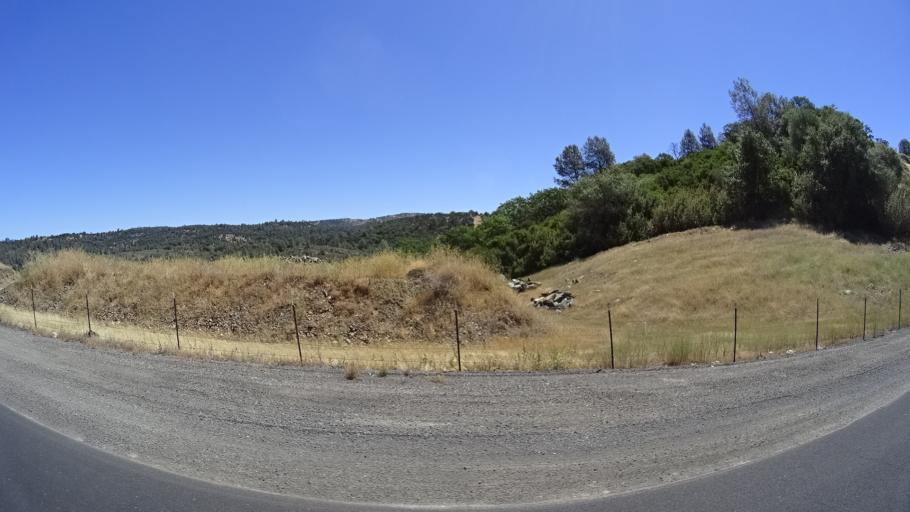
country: US
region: California
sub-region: Calaveras County
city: Copperopolis
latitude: 38.0093
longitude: -120.6438
